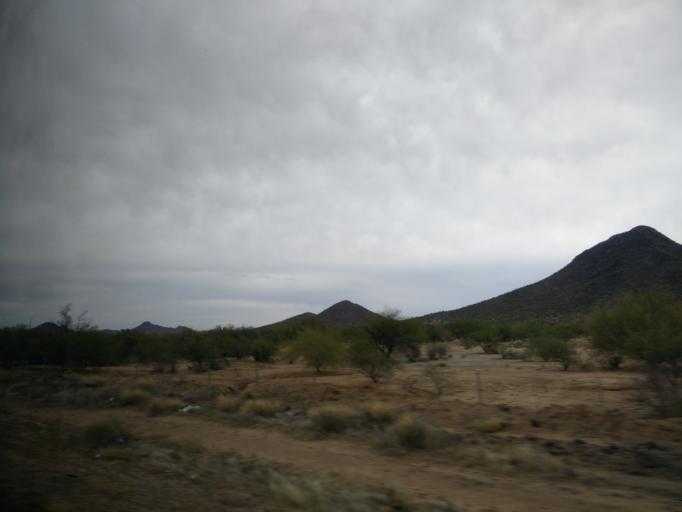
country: MX
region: Sonora
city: Hermosillo
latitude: 28.8174
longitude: -110.9579
